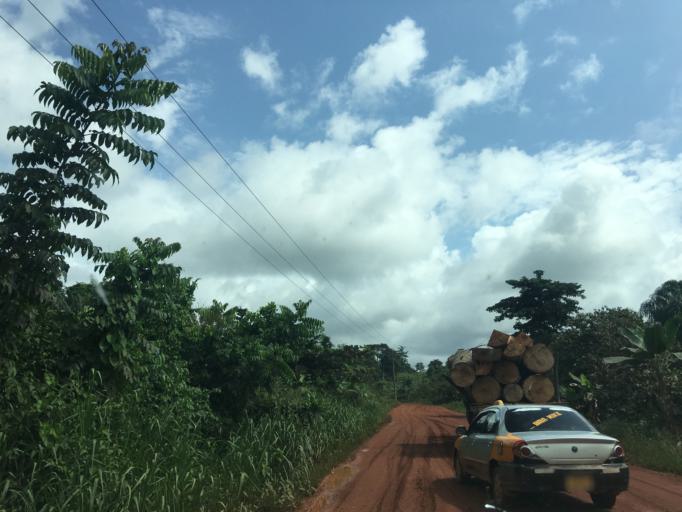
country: GH
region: Western
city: Wassa-Akropong
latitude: 5.7872
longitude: -2.3892
